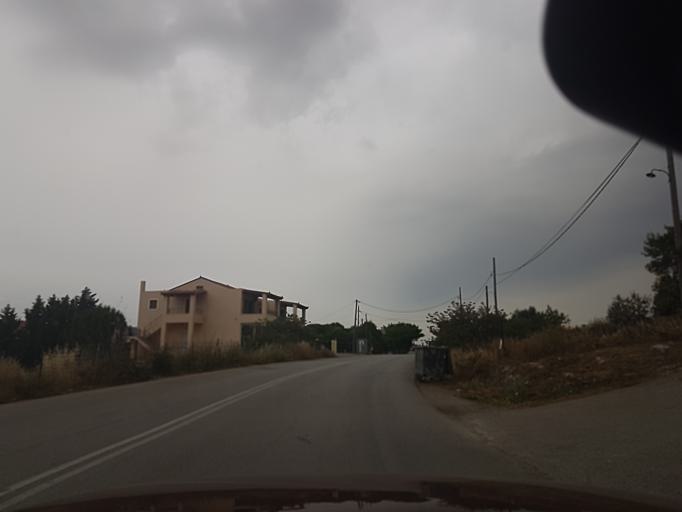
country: GR
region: Central Greece
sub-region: Nomos Evvoias
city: Mytikas
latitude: 38.4595
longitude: 23.6423
